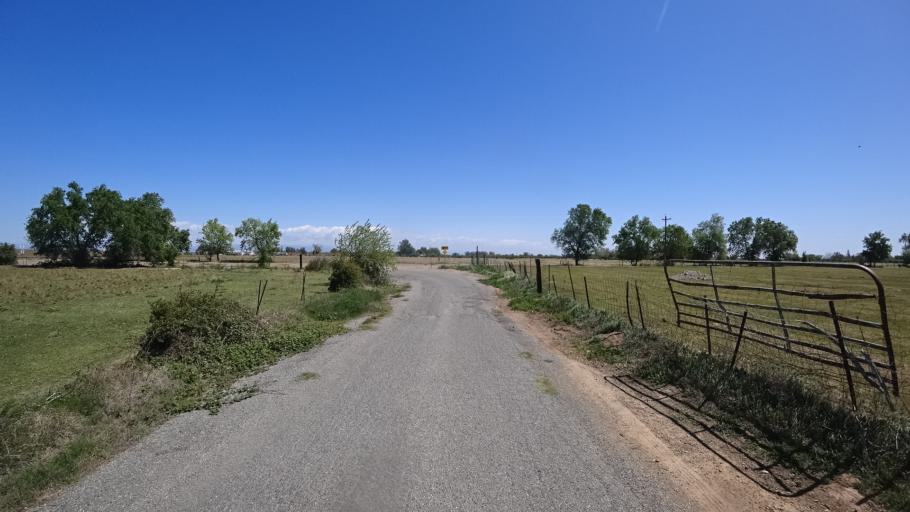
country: US
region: California
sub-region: Glenn County
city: Orland
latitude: 39.7937
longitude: -122.2213
